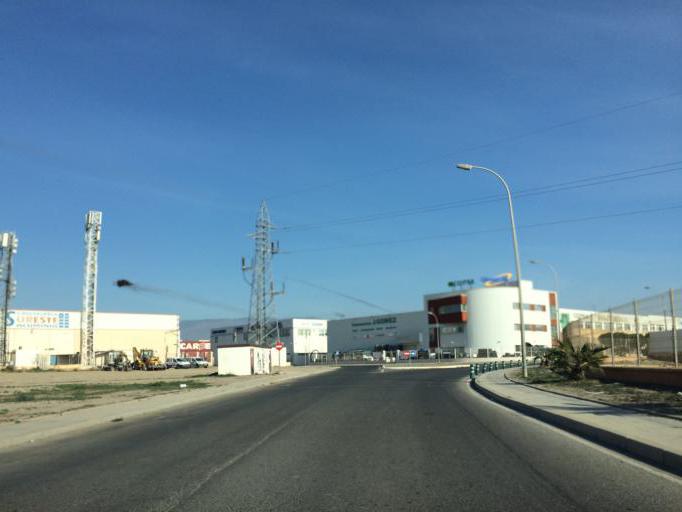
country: ES
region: Andalusia
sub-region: Provincia de Almeria
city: Almeria
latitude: 36.8518
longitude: -2.4316
